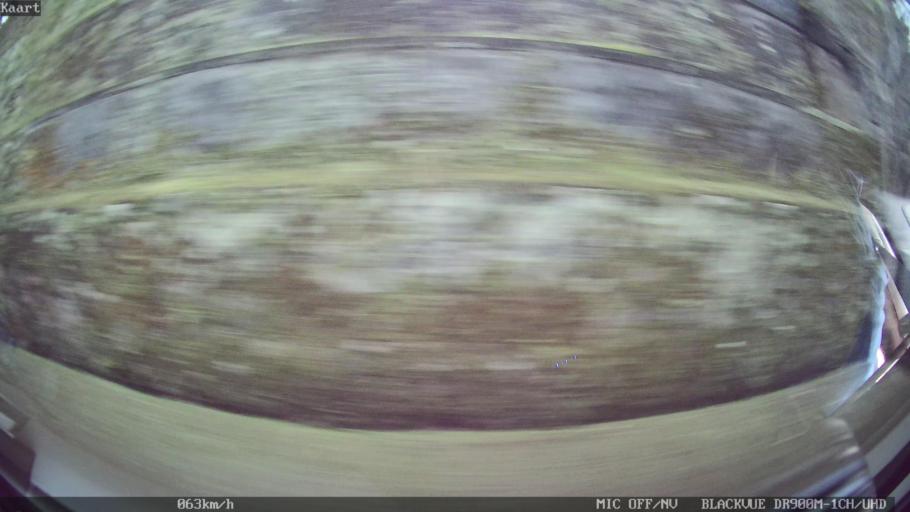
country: ID
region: Bali
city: Penebel
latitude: -8.4158
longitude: 115.1447
